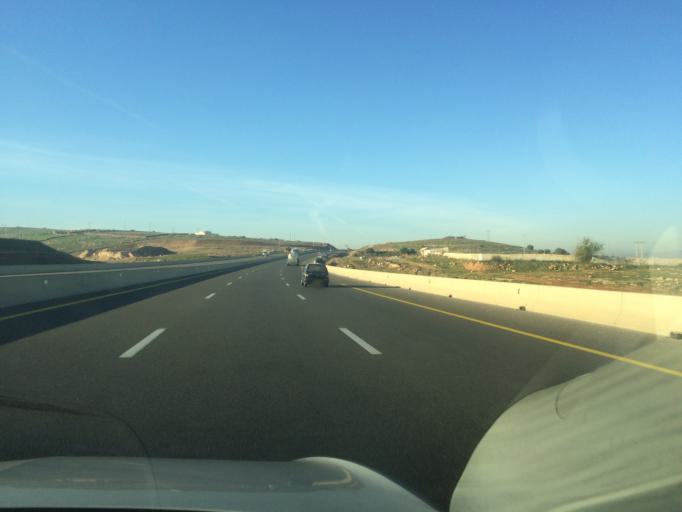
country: DZ
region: Chlef
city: Oued Sly
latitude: 36.0769
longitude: 1.1809
